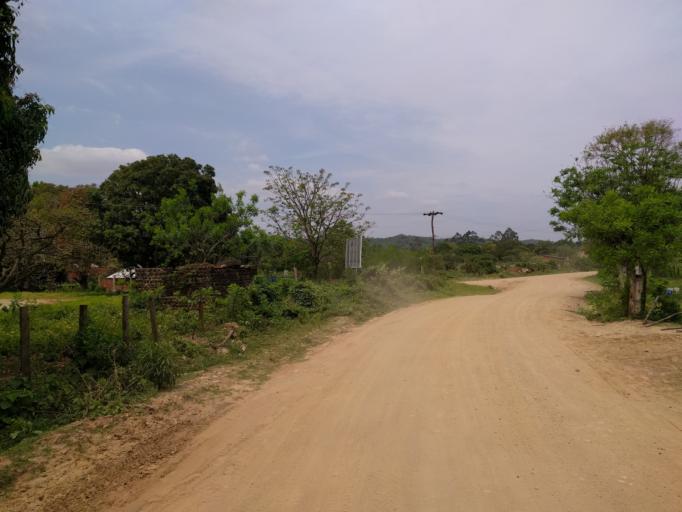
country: BO
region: Santa Cruz
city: Santa Rita
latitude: -17.9398
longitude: -63.3615
